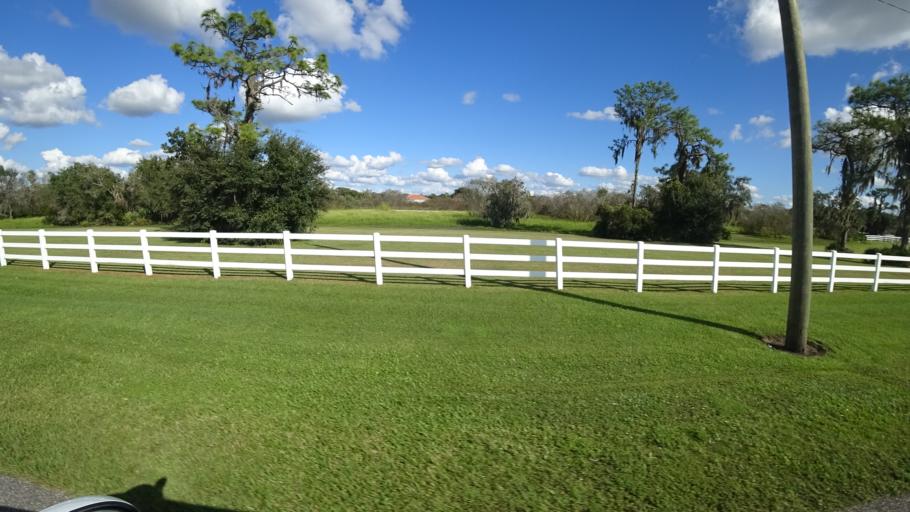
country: US
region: Florida
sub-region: Sarasota County
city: Lake Sarasota
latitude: 27.3458
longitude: -82.2690
